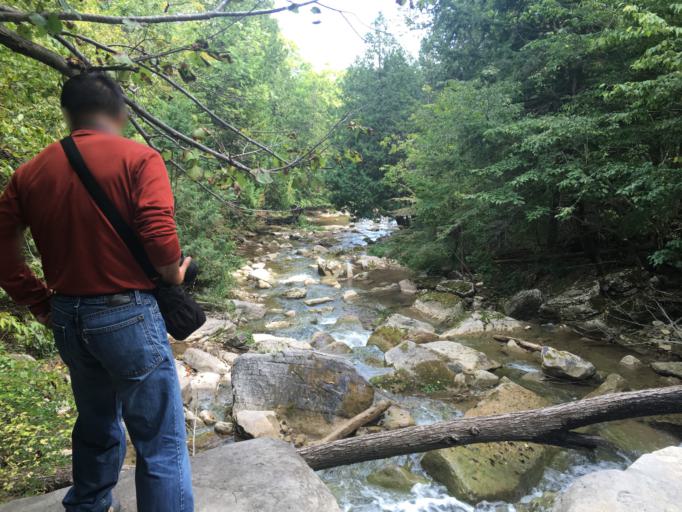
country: US
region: New York
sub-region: Madison County
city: Morrisville
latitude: 42.9512
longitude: -75.6040
